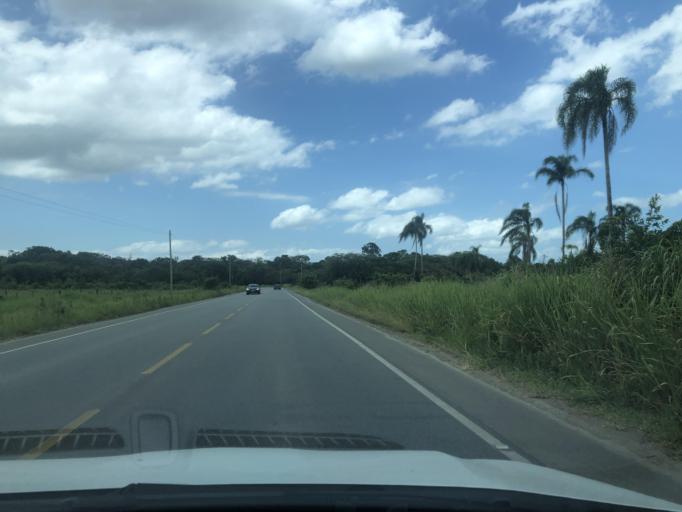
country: BR
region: Santa Catarina
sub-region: Joinville
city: Joinville
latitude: -26.4036
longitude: -48.7576
